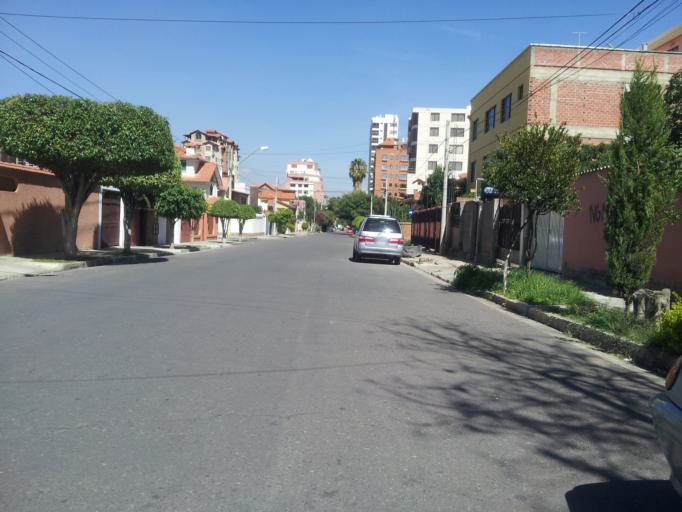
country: BO
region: Cochabamba
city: Cochabamba
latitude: -17.3781
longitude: -66.1739
